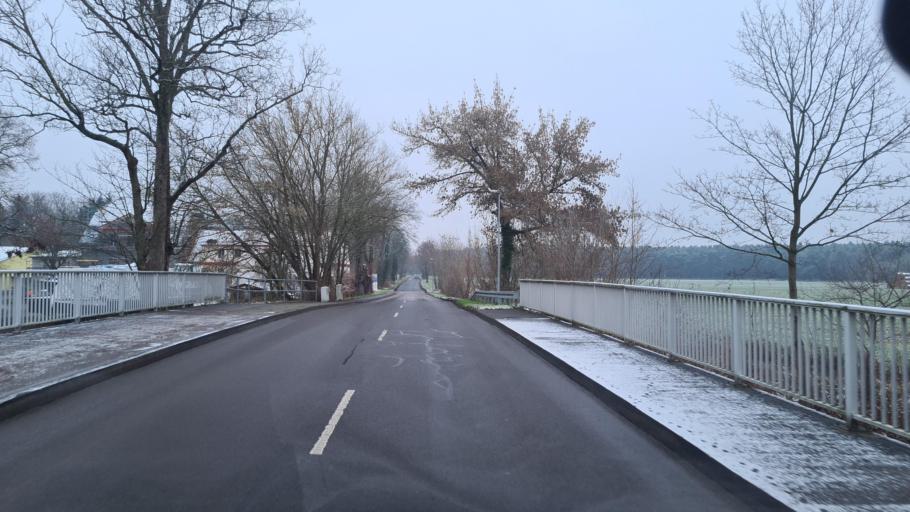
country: DE
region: Brandenburg
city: Storkow
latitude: 52.2568
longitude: 13.8940
